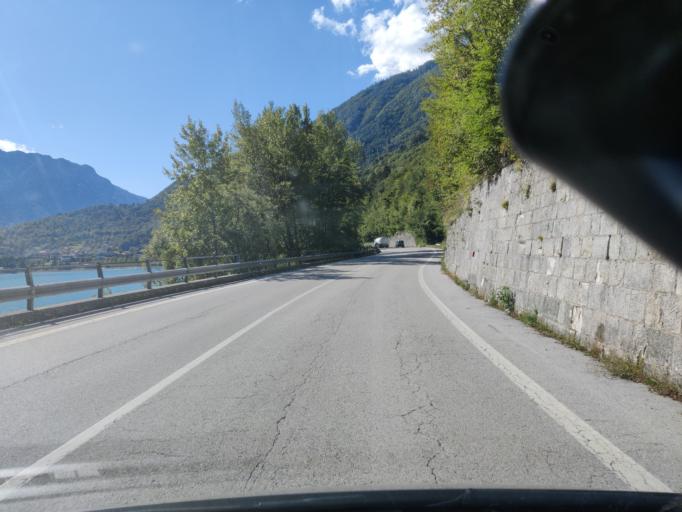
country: IT
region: Veneto
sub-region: Provincia di Belluno
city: Farra d'Alpago
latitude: 46.1044
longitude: 12.3277
